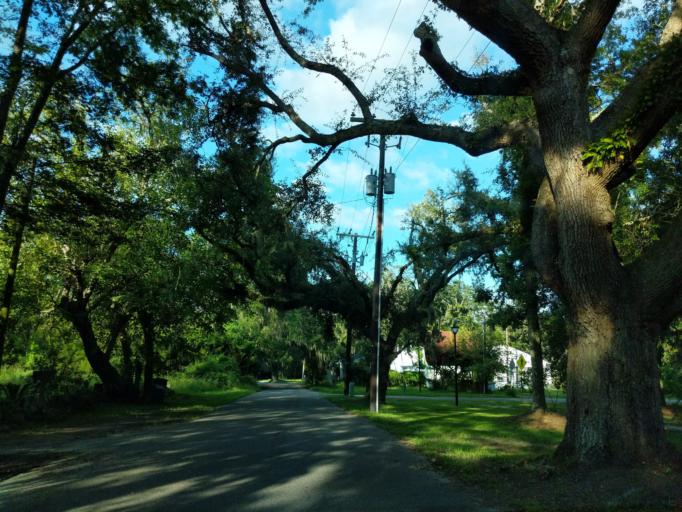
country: US
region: South Carolina
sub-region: Charleston County
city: Awendaw
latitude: 33.0890
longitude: -79.4630
